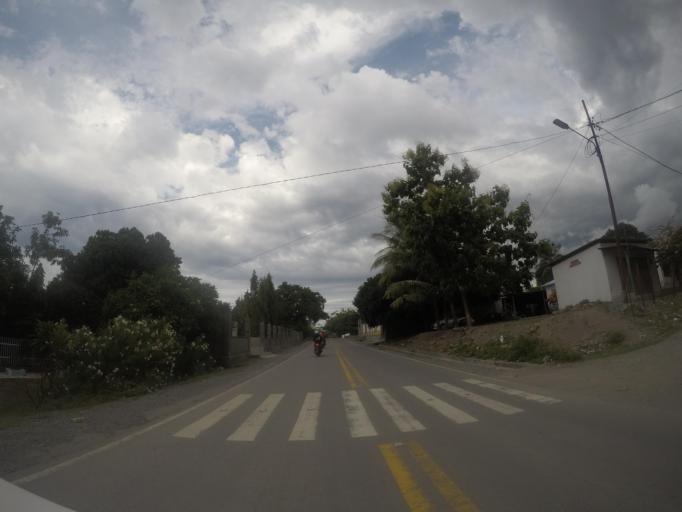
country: TL
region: Liquica
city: Liquica
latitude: -8.5920
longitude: 125.3288
